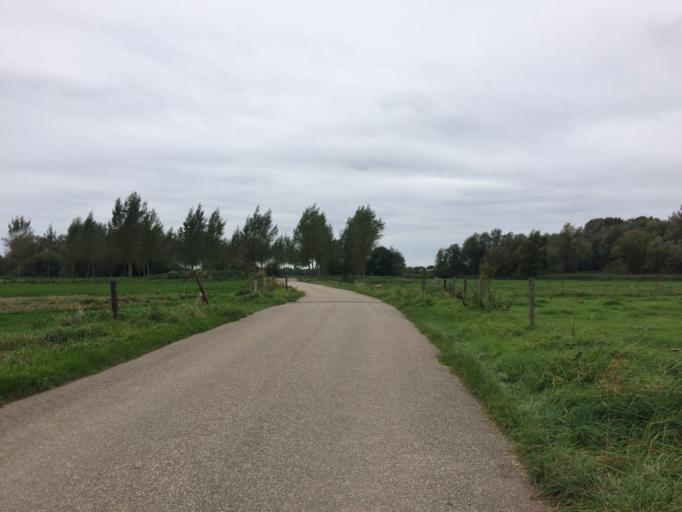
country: NL
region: Gelderland
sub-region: Gemeente Maasdriel
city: Hedel
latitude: 51.7194
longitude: 5.2538
